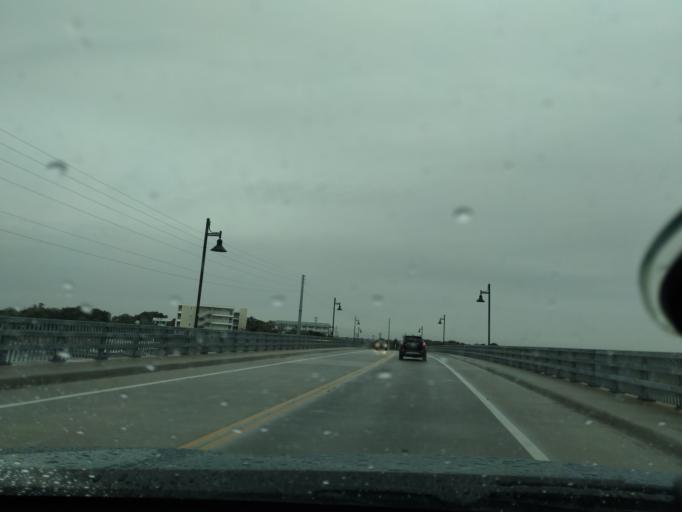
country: US
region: South Carolina
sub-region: Charleston County
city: Folly Beach
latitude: 32.6608
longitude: -79.9431
